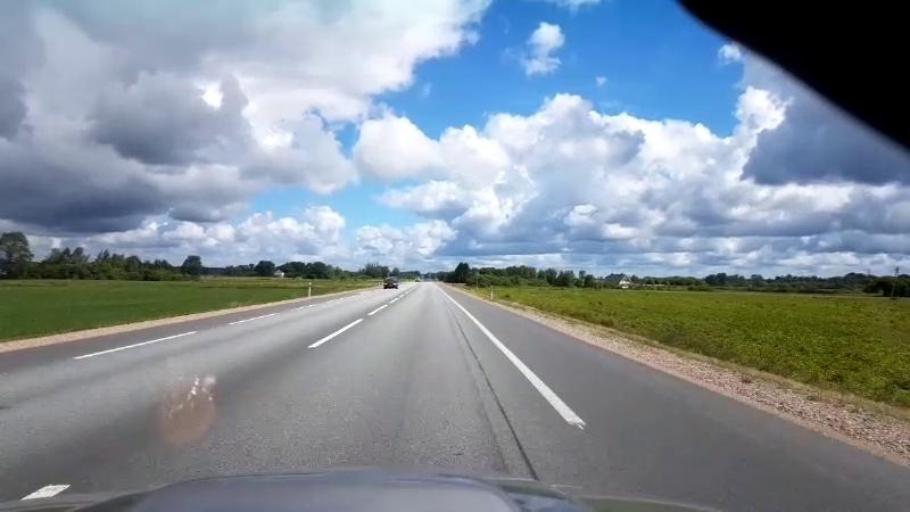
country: LV
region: Lecava
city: Iecava
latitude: 56.6136
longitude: 24.2154
